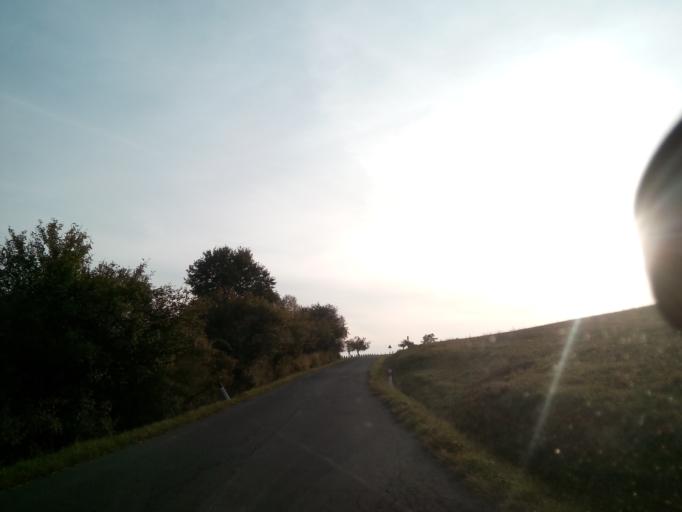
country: SK
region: Presovsky
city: Svidnik
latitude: 49.3790
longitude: 21.4847
